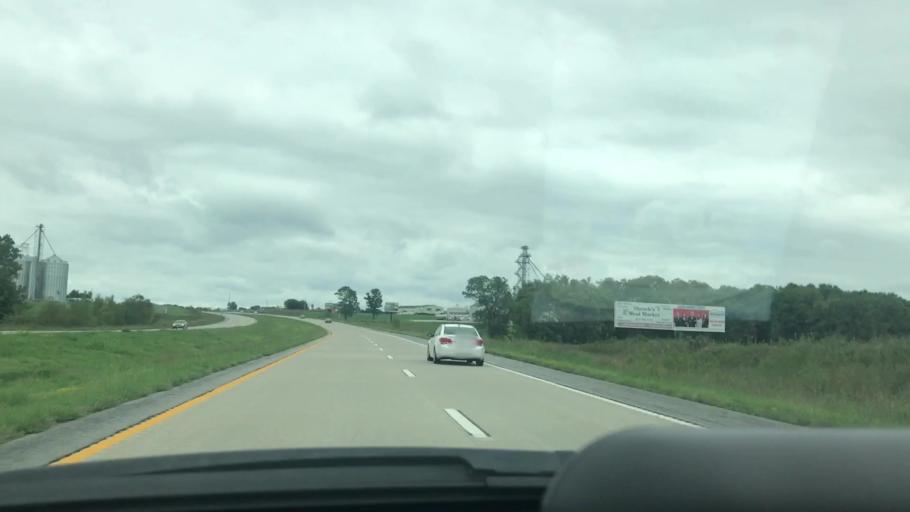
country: US
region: Missouri
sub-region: Dallas County
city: Buffalo
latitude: 37.5916
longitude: -93.1285
